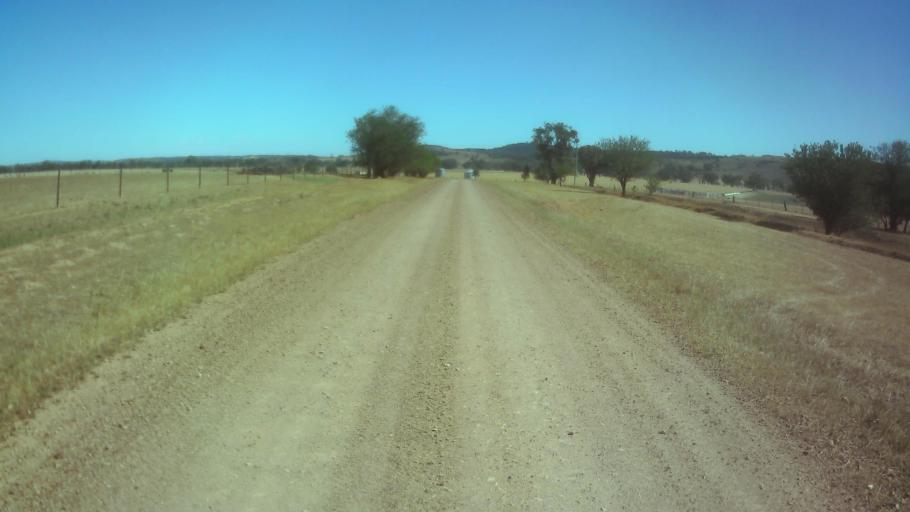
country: AU
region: New South Wales
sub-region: Weddin
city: Grenfell
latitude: -33.9559
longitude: 148.3025
